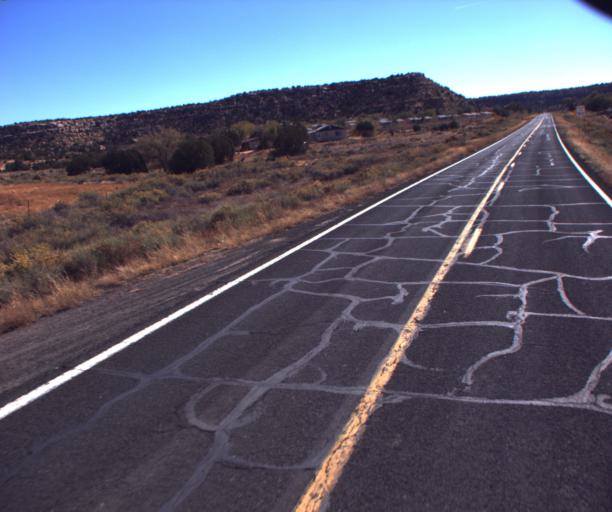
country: US
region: Arizona
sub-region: Navajo County
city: First Mesa
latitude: 35.8271
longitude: -110.2217
